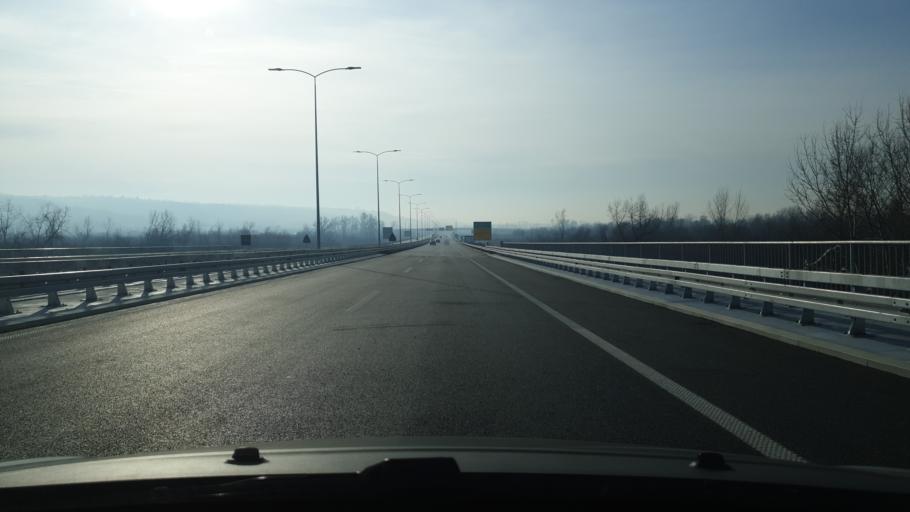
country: RS
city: Baric
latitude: 44.6600
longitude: 20.2399
